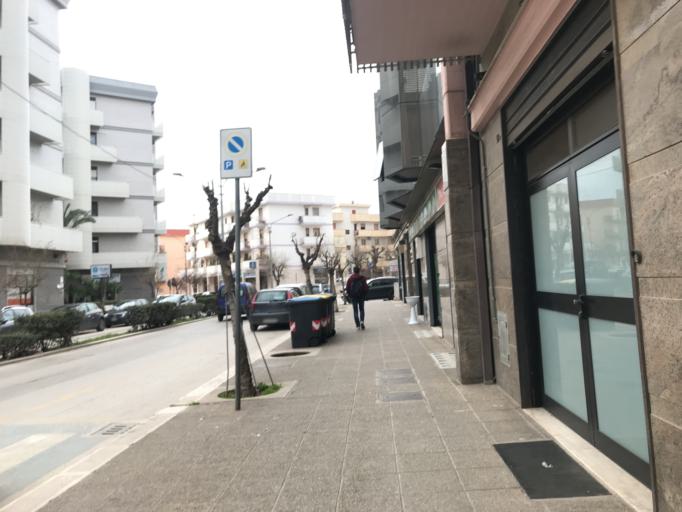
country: IT
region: Apulia
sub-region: Provincia di Bari
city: Corato
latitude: 41.1572
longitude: 16.4155
